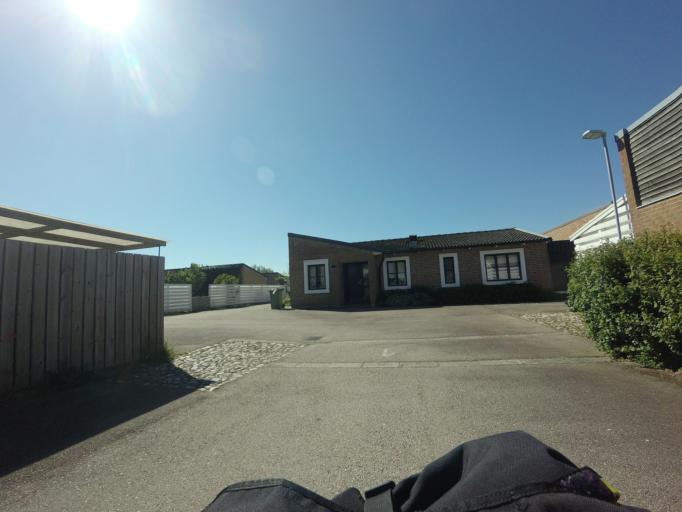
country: SE
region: Skane
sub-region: Hoganas Kommun
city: Hoganas
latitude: 56.1784
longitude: 12.5660
